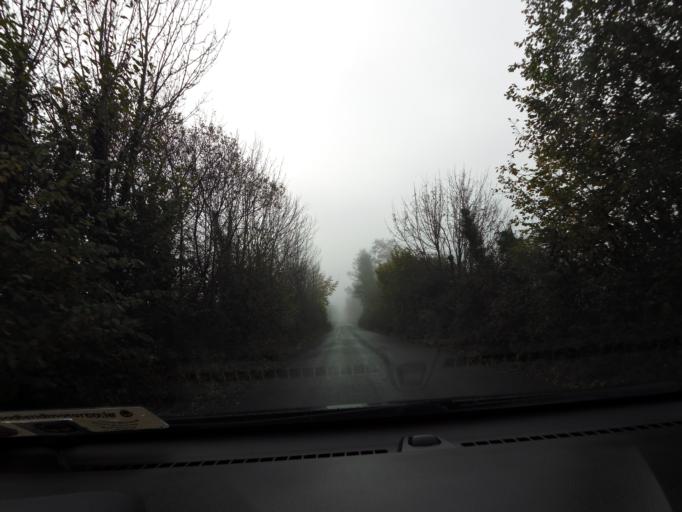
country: IE
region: Leinster
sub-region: An Iarmhi
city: Moate
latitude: 53.3861
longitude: -7.8056
